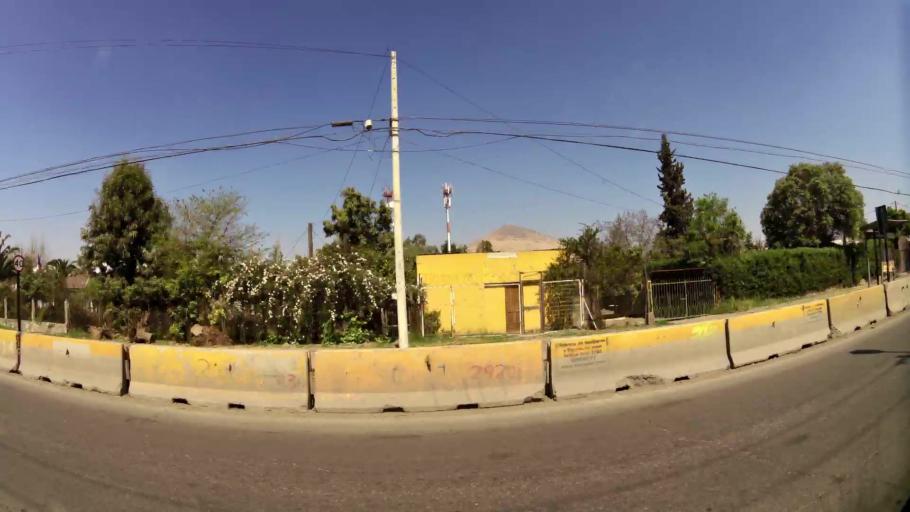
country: CL
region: Santiago Metropolitan
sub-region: Provincia de Santiago
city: Lo Prado
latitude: -33.3663
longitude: -70.7111
